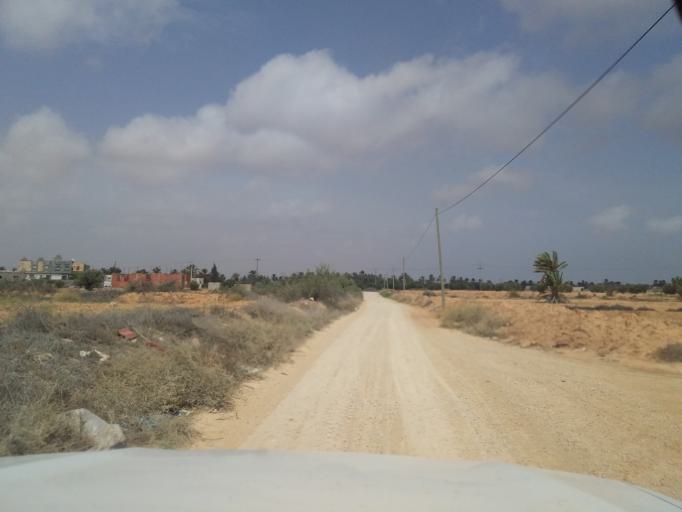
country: TN
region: Qabis
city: Gabes
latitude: 33.6289
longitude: 10.3072
